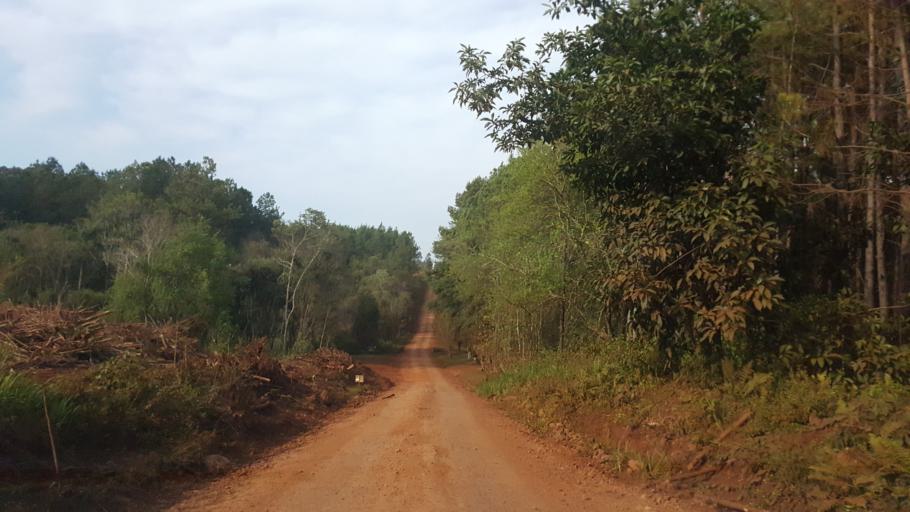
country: AR
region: Misiones
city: Capiovi
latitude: -26.9161
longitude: -55.1165
